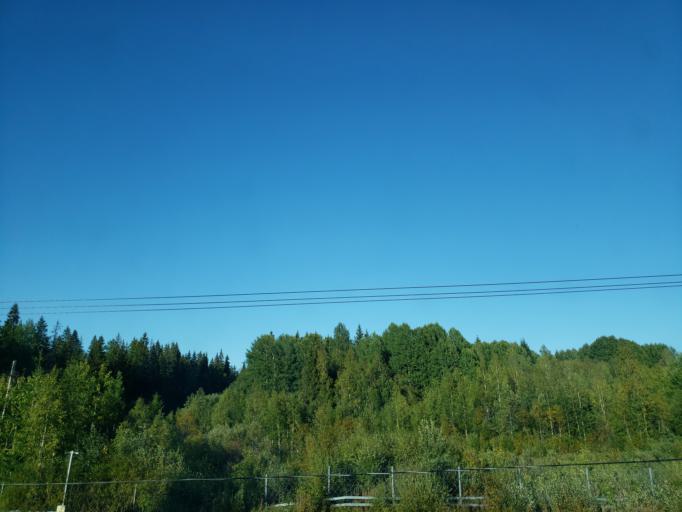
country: FI
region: South Karelia
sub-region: Lappeenranta
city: Nuijamaa
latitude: 60.8479
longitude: 28.3686
